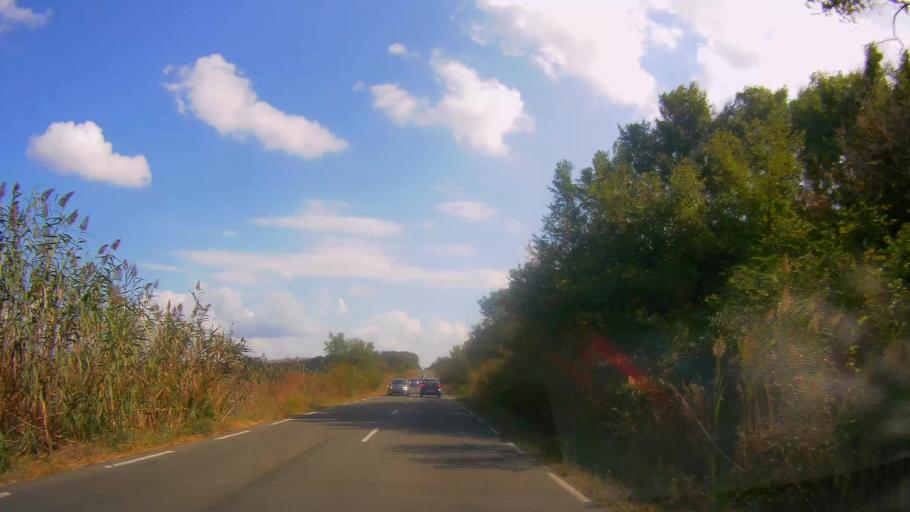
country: BG
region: Burgas
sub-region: Obshtina Kameno
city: Kameno
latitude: 42.4857
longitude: 27.3419
